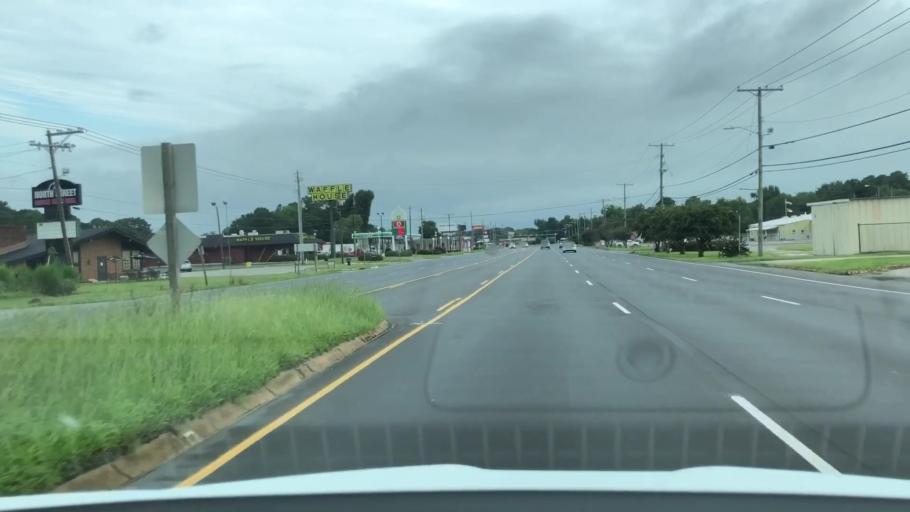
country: US
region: North Carolina
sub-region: Lenoir County
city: Kinston
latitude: 35.2383
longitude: -77.5749
